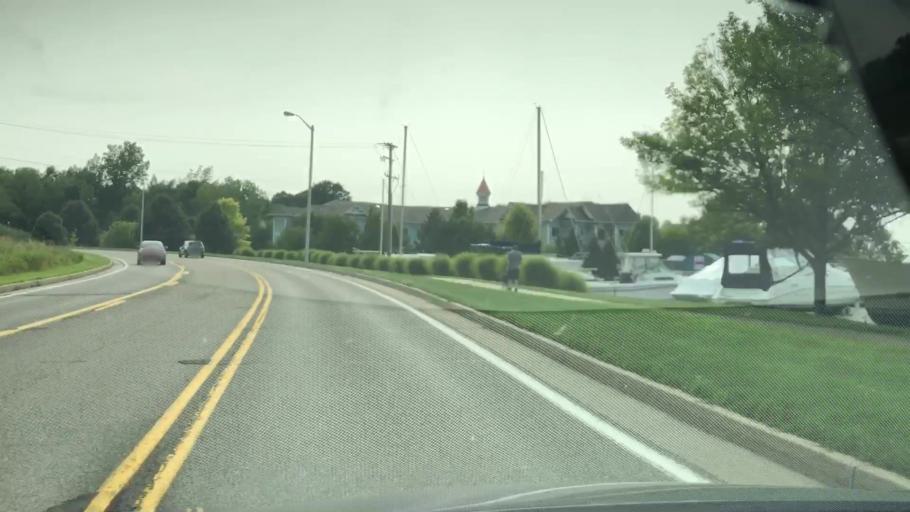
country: US
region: Pennsylvania
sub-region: Erie County
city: Erie
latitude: 42.1273
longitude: -80.1083
